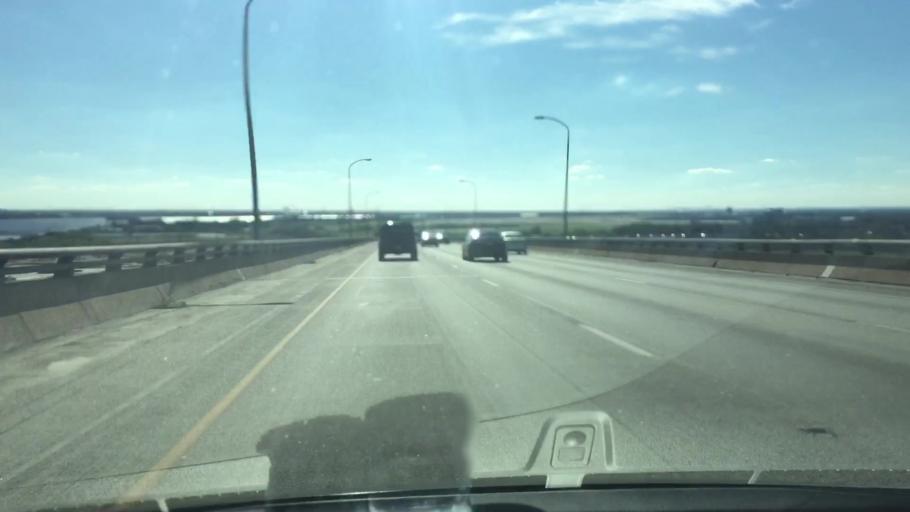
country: US
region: New Jersey
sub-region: Gloucester County
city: National Park
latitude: 39.8906
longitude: -75.2008
